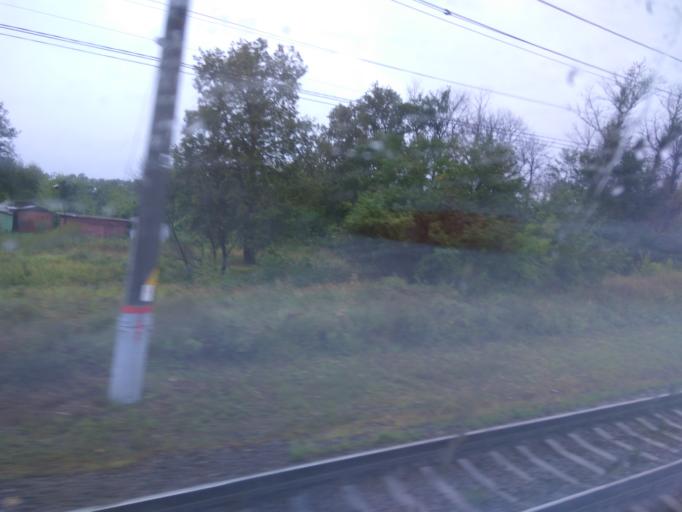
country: RU
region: Moskovskaya
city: Zhilevo
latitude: 54.9825
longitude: 38.0330
